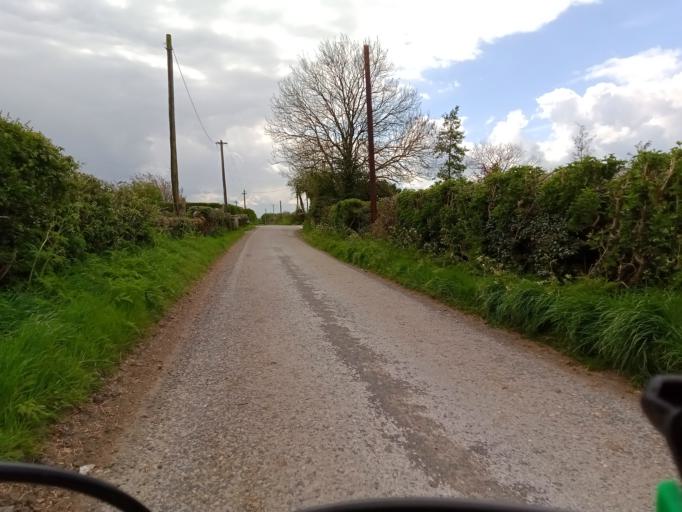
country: IE
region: Leinster
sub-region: Kilkenny
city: Kilkenny
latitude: 52.6242
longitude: -7.2923
